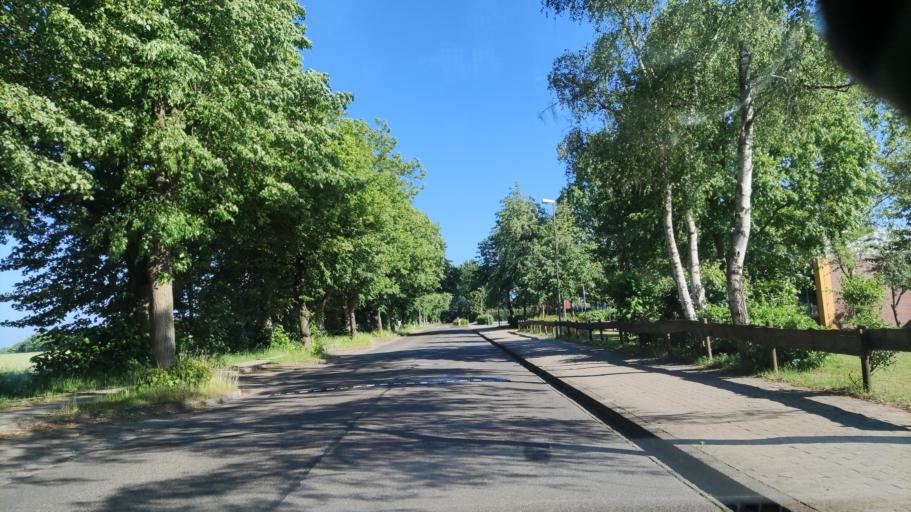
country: DE
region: Lower Saxony
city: Stelle
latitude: 53.3670
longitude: 10.1268
